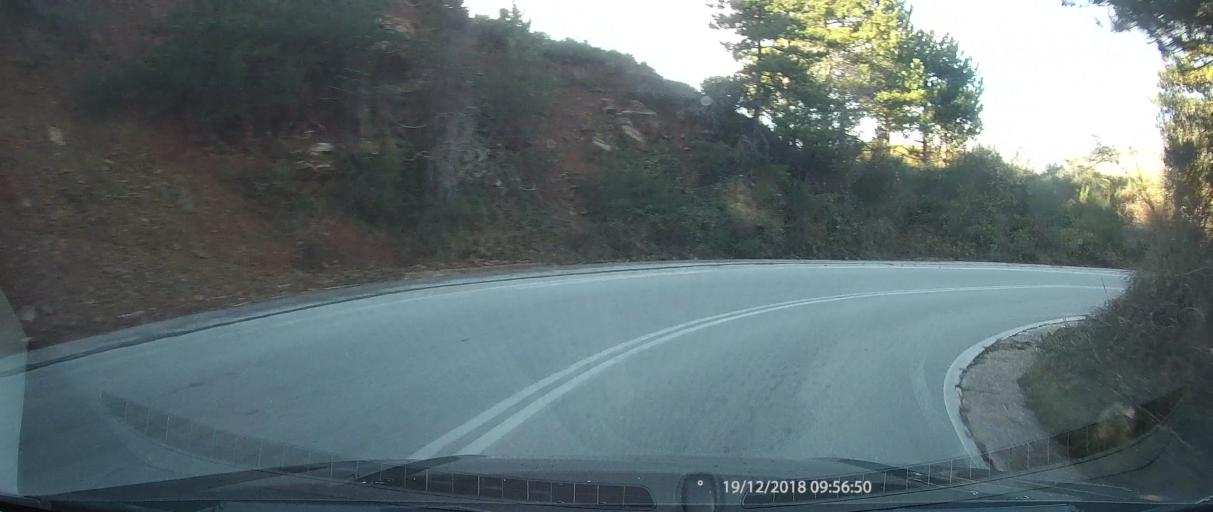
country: GR
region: Peloponnese
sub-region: Nomos Messinias
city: Paralia Vergas
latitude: 37.0849
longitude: 22.2355
